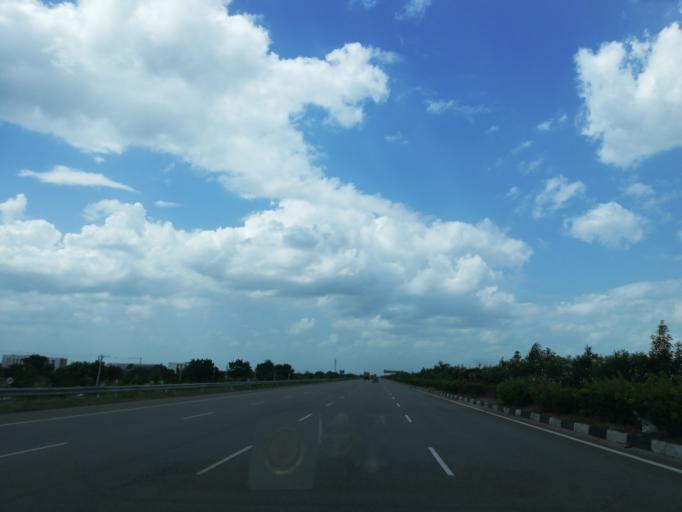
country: IN
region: Telangana
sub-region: Medak
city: Serilingampalle
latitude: 17.4784
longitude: 78.2471
